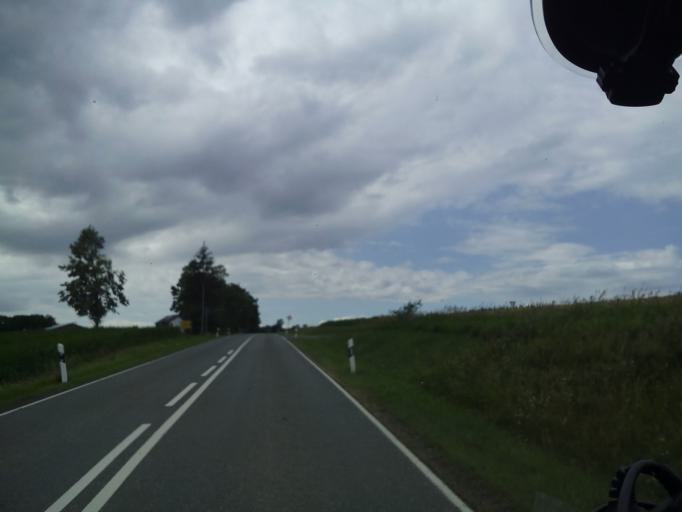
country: DE
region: Bavaria
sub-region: Upper Franconia
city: Sonnefeld
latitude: 50.2405
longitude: 11.1140
